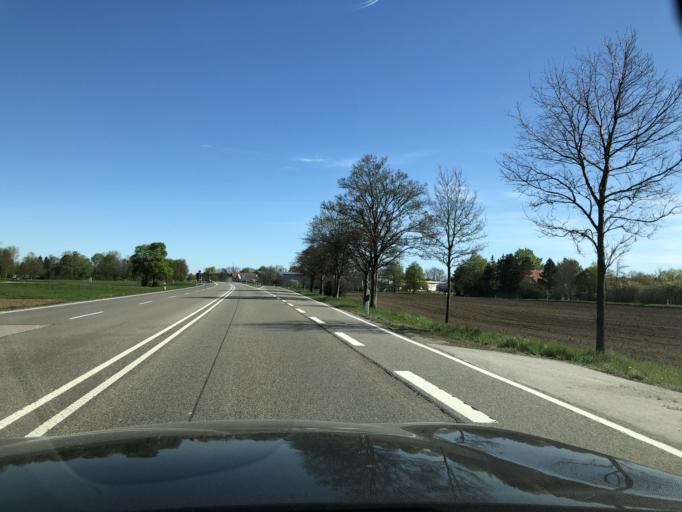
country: DE
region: Bavaria
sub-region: Swabia
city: Jengen
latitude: 48.0014
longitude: 10.7189
